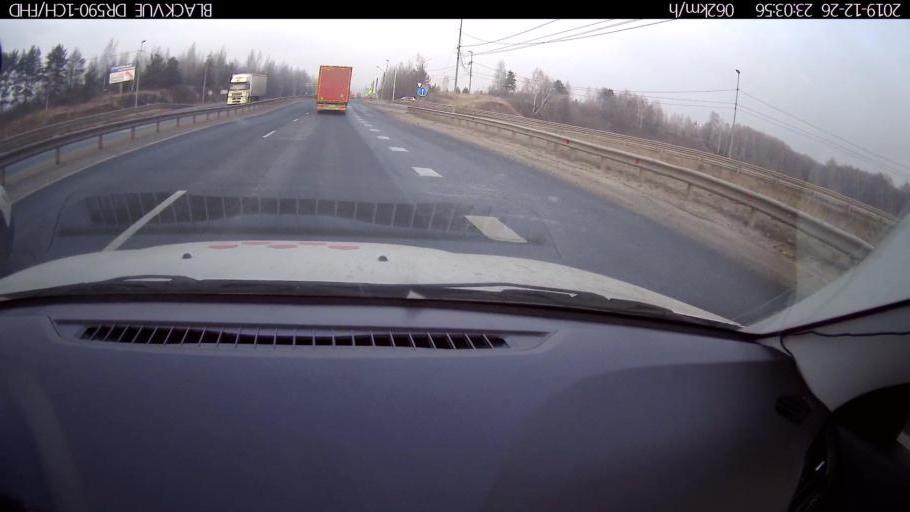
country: RU
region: Nizjnij Novgorod
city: Burevestnik
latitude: 56.1742
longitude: 43.7479
